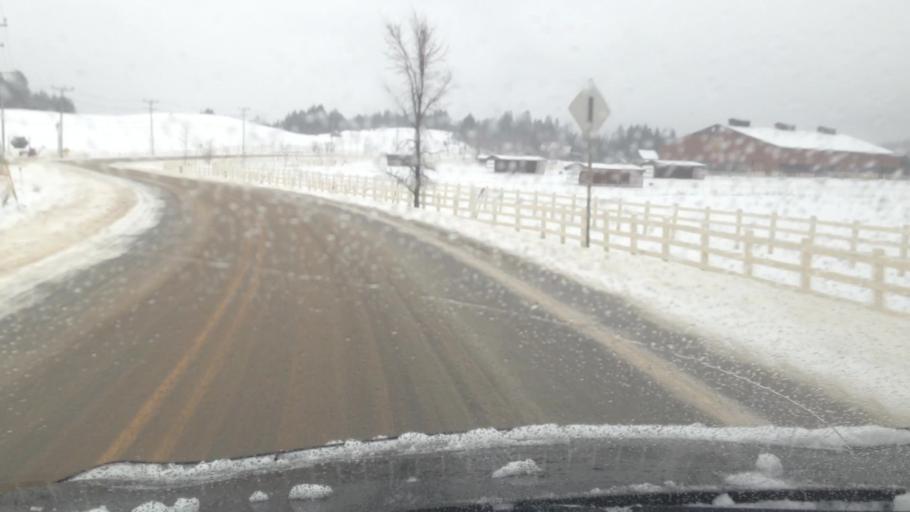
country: CA
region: Quebec
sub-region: Laurentides
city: Mont-Tremblant
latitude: 46.0396
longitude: -74.6025
